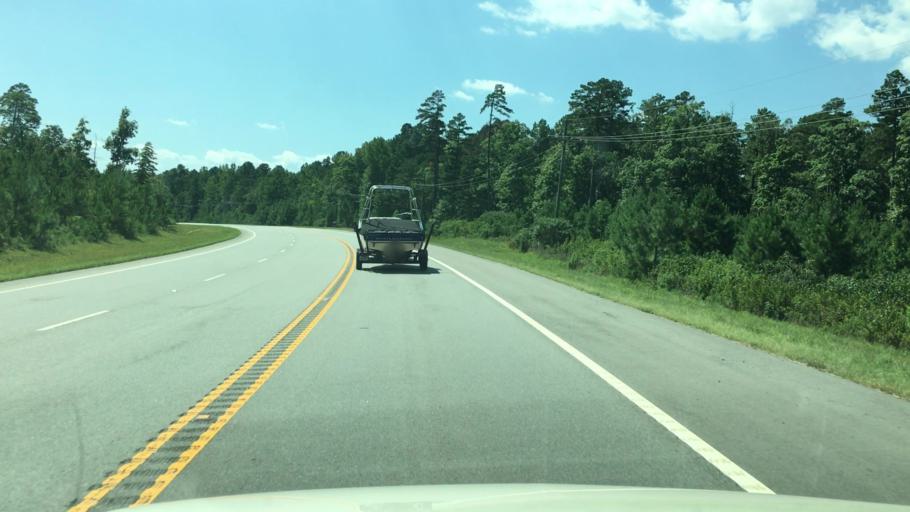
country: US
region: Arkansas
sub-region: Garland County
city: Piney
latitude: 34.5224
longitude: -93.3189
